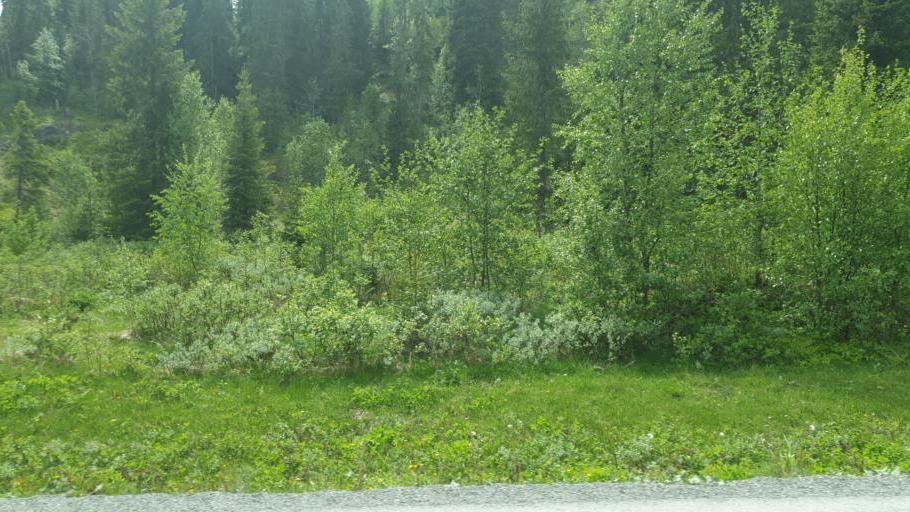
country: NO
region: Nord-Trondelag
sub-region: Leksvik
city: Leksvik
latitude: 63.6911
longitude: 10.5165
